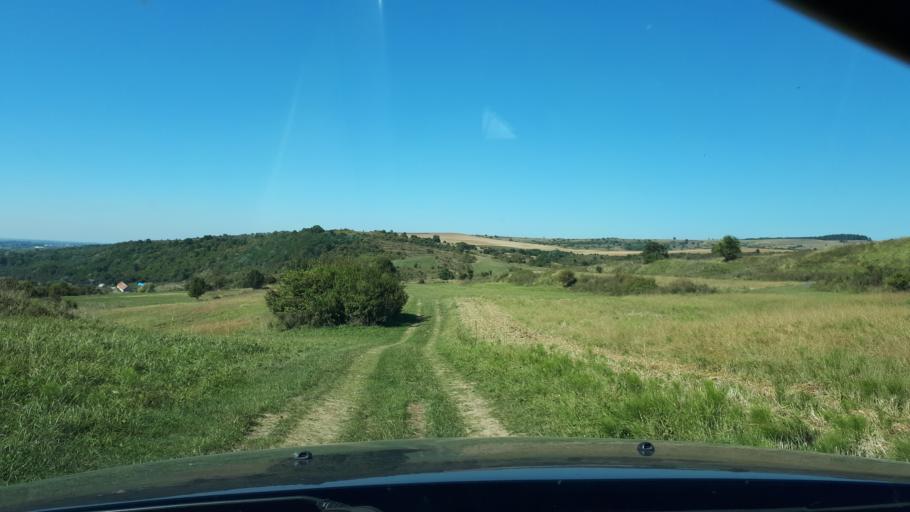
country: RO
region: Brasov
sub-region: Comuna Mandra
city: Mandra
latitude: 45.8559
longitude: 25.0659
